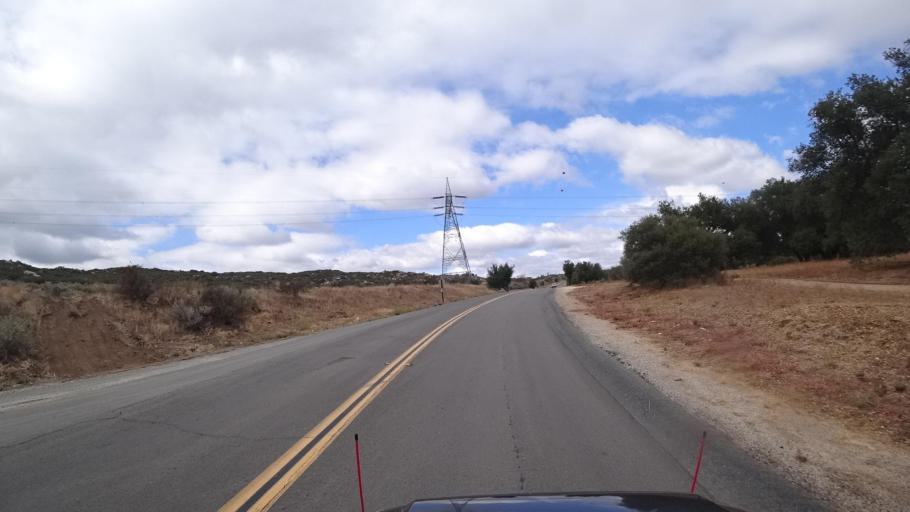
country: US
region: California
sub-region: San Diego County
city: Campo
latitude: 32.6613
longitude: -116.5016
